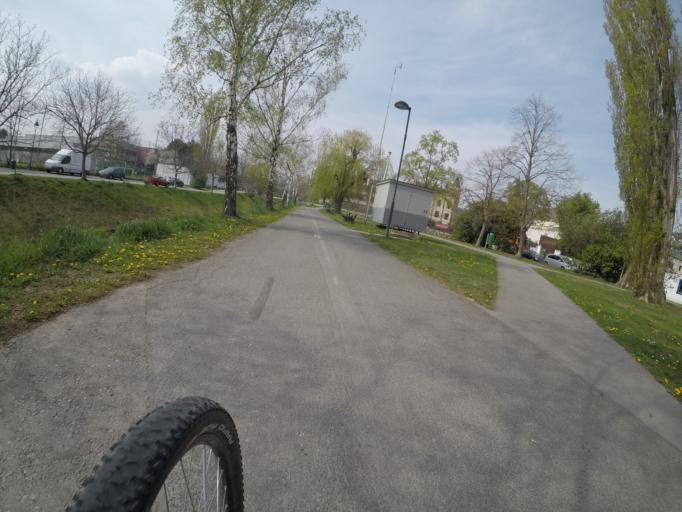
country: AT
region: Lower Austria
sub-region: Politischer Bezirk Modling
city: Modling
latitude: 48.0855
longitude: 16.3015
